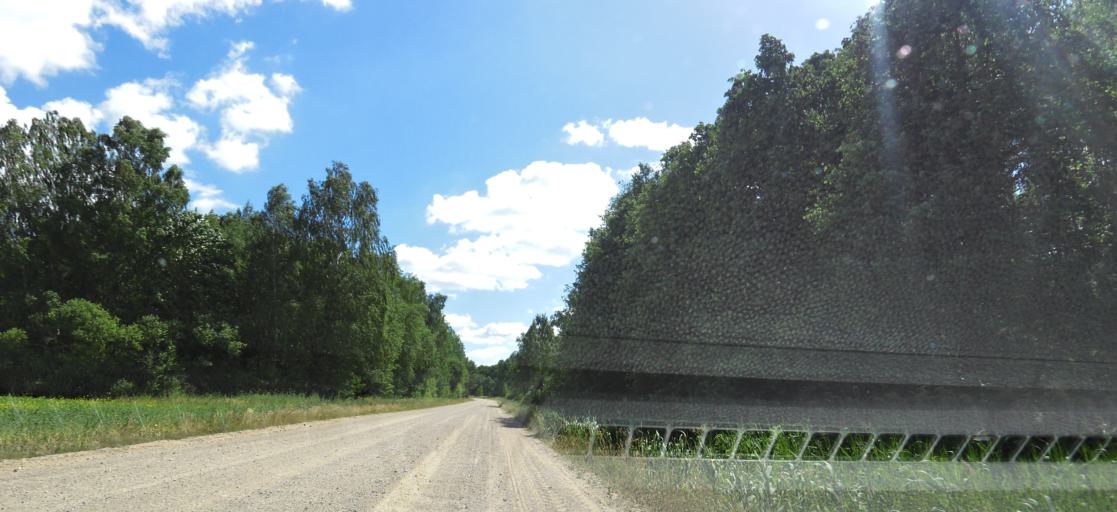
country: LT
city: Vabalninkas
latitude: 56.0294
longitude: 24.9290
